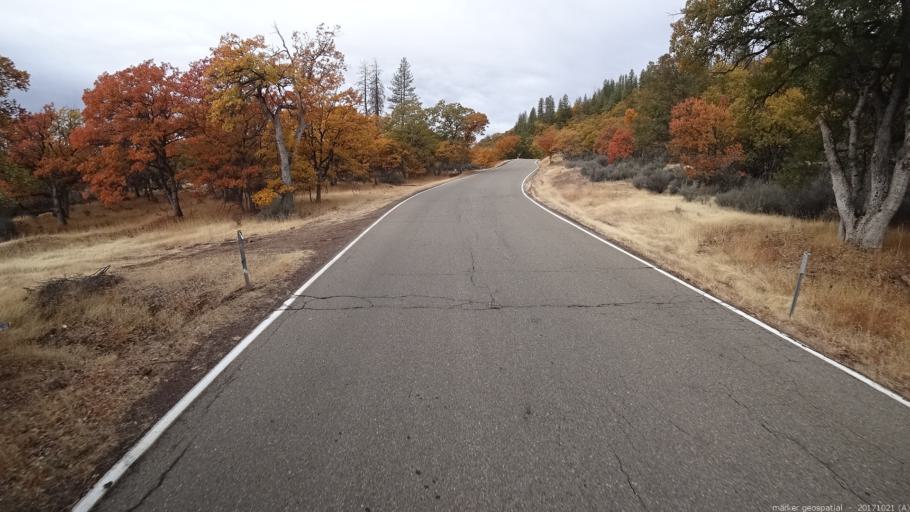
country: US
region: California
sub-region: Shasta County
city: Burney
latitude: 41.0419
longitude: -121.6561
